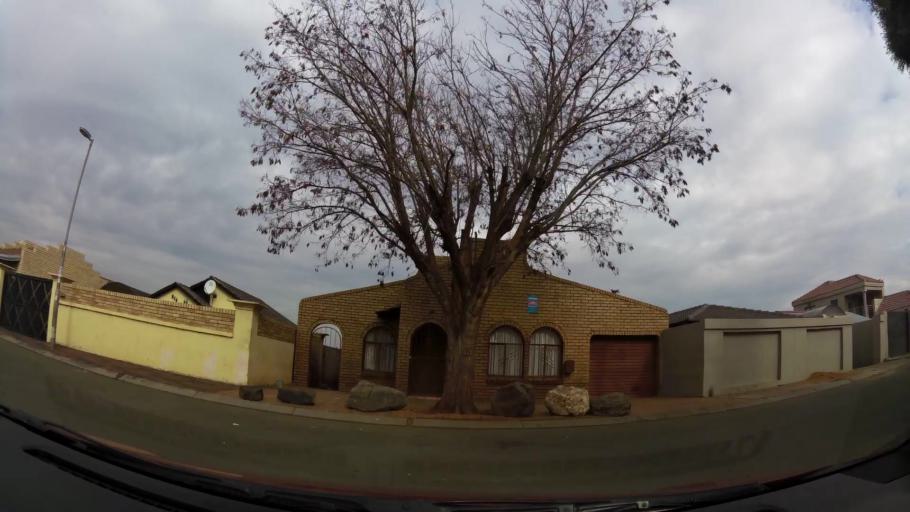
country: ZA
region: Gauteng
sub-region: City of Johannesburg Metropolitan Municipality
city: Soweto
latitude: -26.2749
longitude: 27.8294
